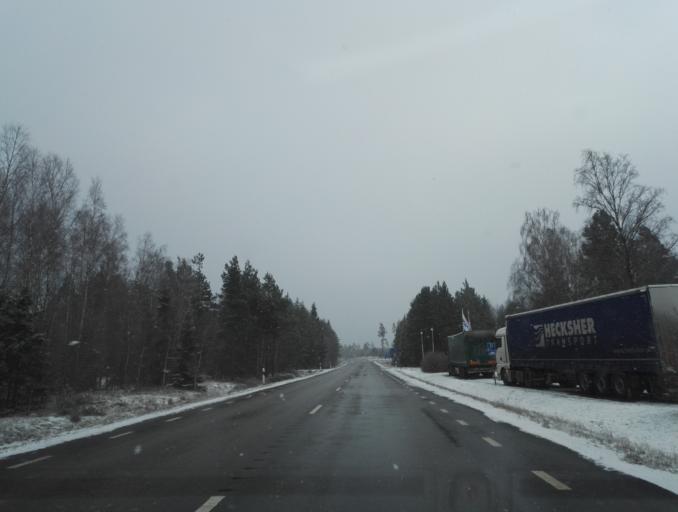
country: SE
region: Kronoberg
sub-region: Uppvidinge Kommun
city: Lenhovda
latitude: 56.9230
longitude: 15.3618
